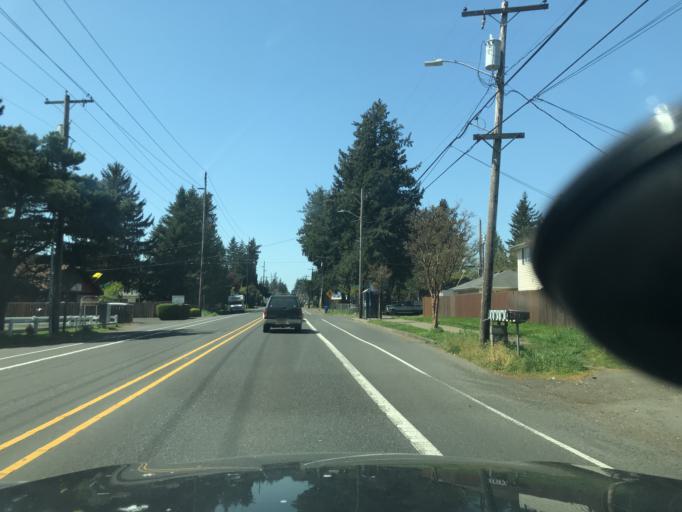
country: US
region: Oregon
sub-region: Multnomah County
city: Lents
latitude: 45.4974
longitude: -122.5304
